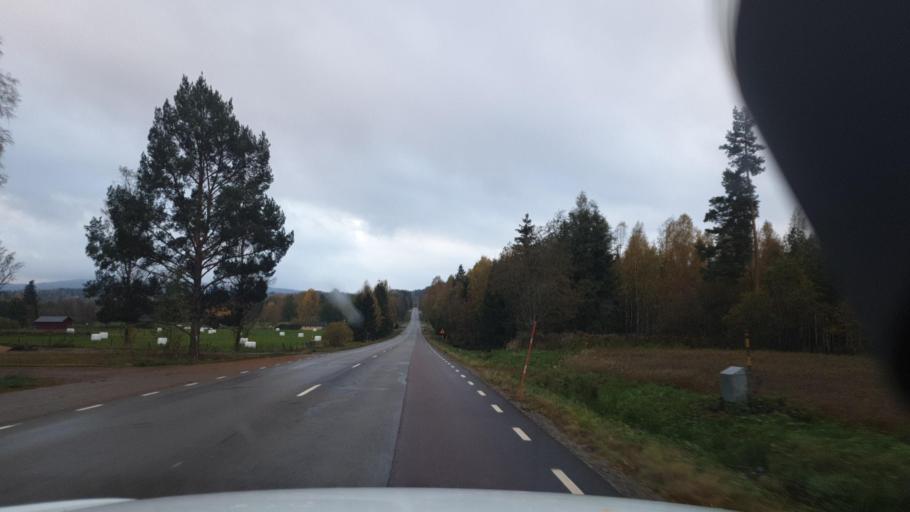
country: SE
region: Vaermland
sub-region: Arvika Kommun
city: Arvika
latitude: 59.6875
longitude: 12.6326
